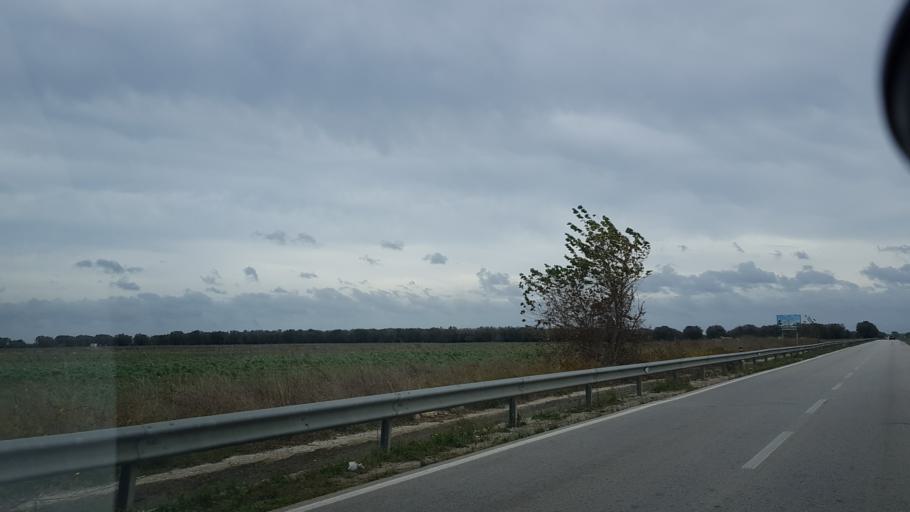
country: IT
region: Apulia
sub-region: Provincia di Brindisi
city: San Pancrazio Salentino
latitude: 40.4093
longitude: 17.8764
